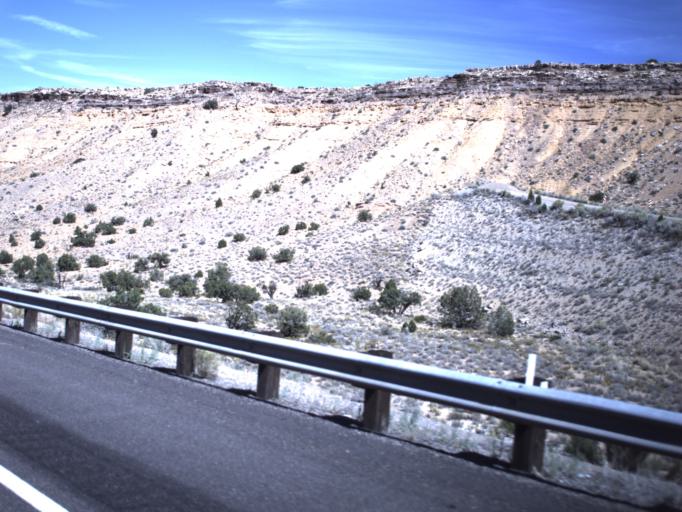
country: US
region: Utah
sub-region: Emery County
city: Castle Dale
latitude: 38.9325
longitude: -110.4888
